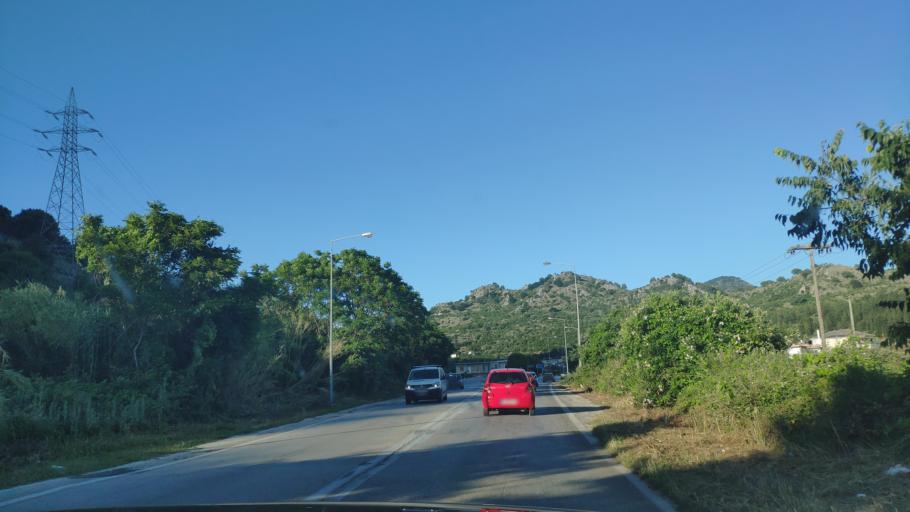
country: GR
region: Epirus
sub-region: Nomos Prevezis
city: Louros
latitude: 39.1788
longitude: 20.7809
